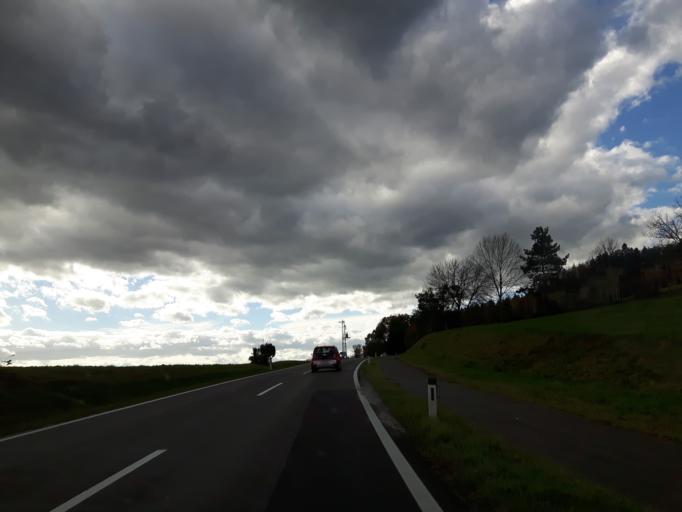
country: AT
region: Styria
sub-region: Politischer Bezirk Suedoststeiermark
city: Kirchbach in Steiermark
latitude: 46.9093
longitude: 15.6711
